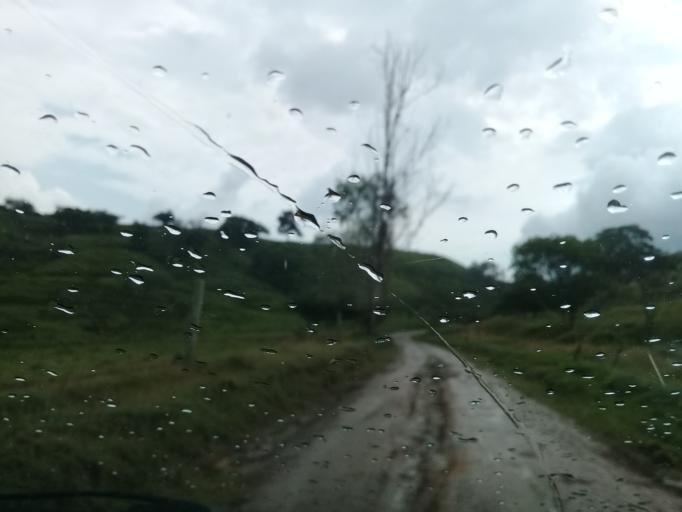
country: CO
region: Cundinamarca
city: Guaduas
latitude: 5.0962
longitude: -74.6063
